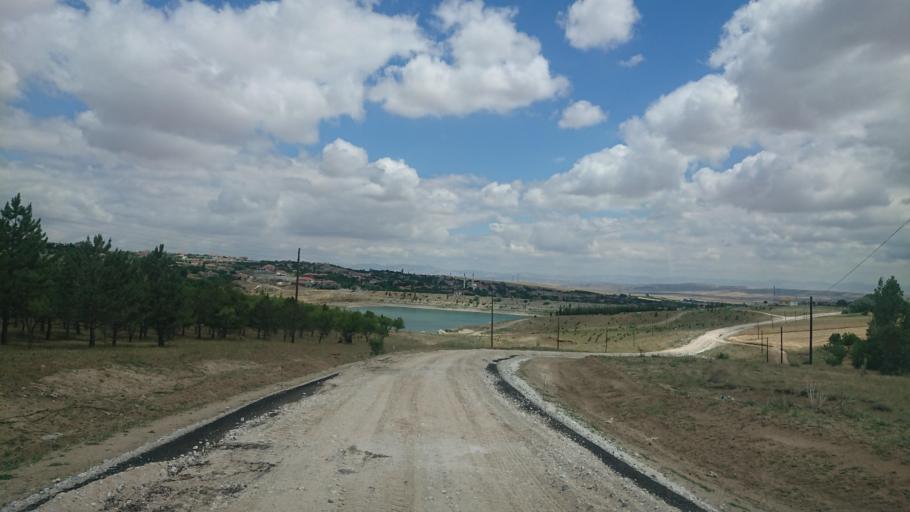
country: TR
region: Aksaray
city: Agacoren
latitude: 38.8605
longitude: 33.9478
